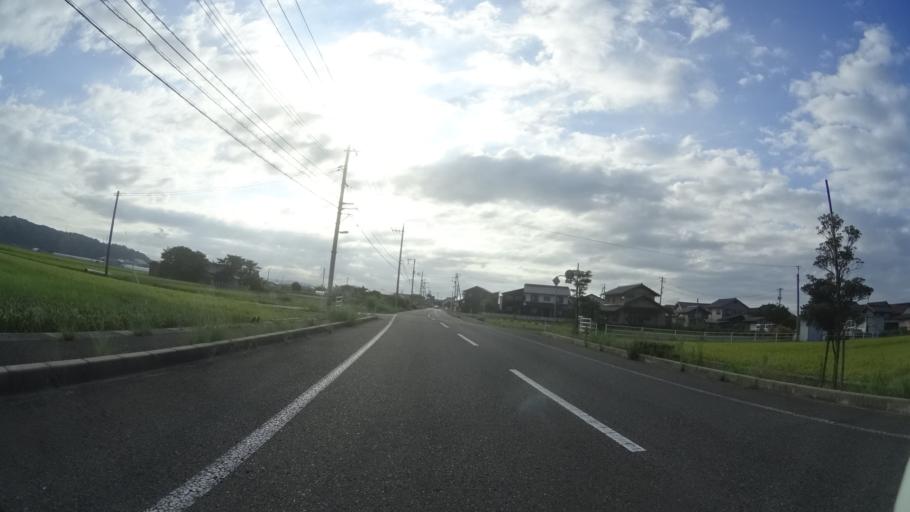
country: JP
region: Tottori
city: Kurayoshi
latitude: 35.4913
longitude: 133.8743
